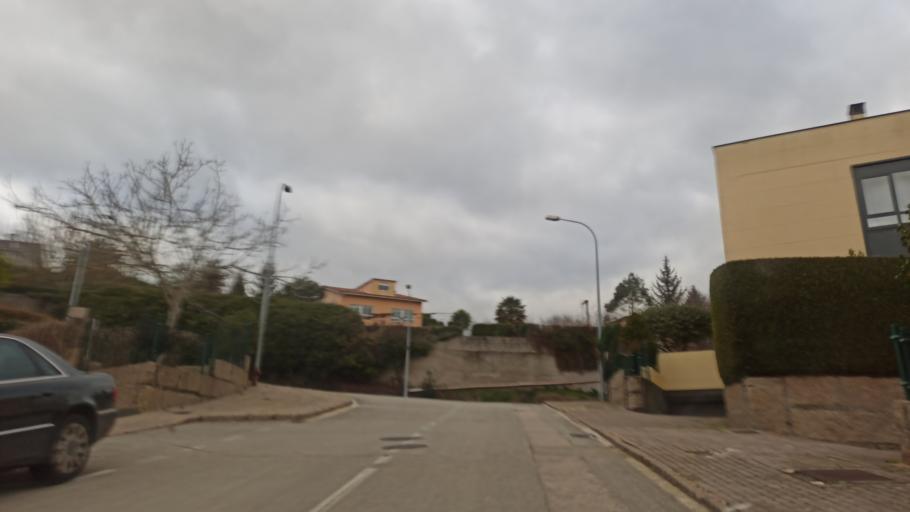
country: ES
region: Galicia
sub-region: Provincia da Coruna
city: Oleiros
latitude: 43.3284
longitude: -8.3479
